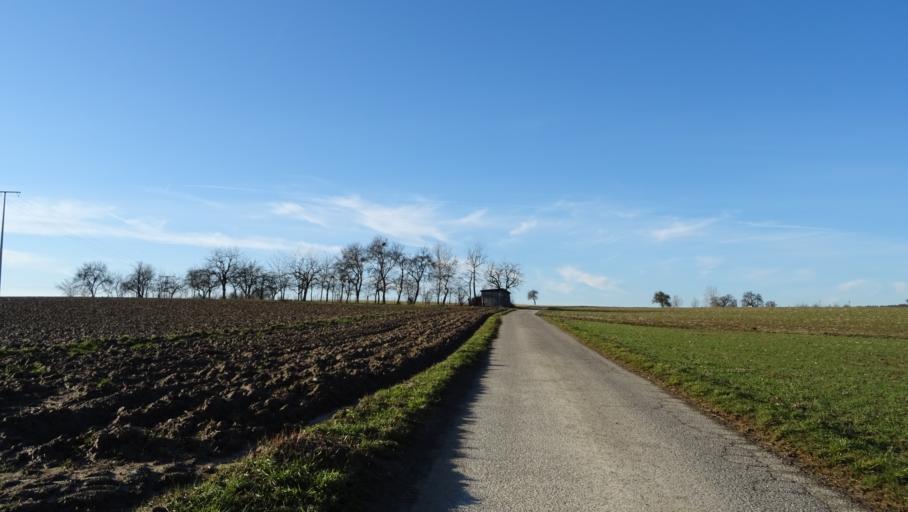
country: DE
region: Baden-Wuerttemberg
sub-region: Karlsruhe Region
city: Billigheim
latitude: 49.4154
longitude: 9.2664
